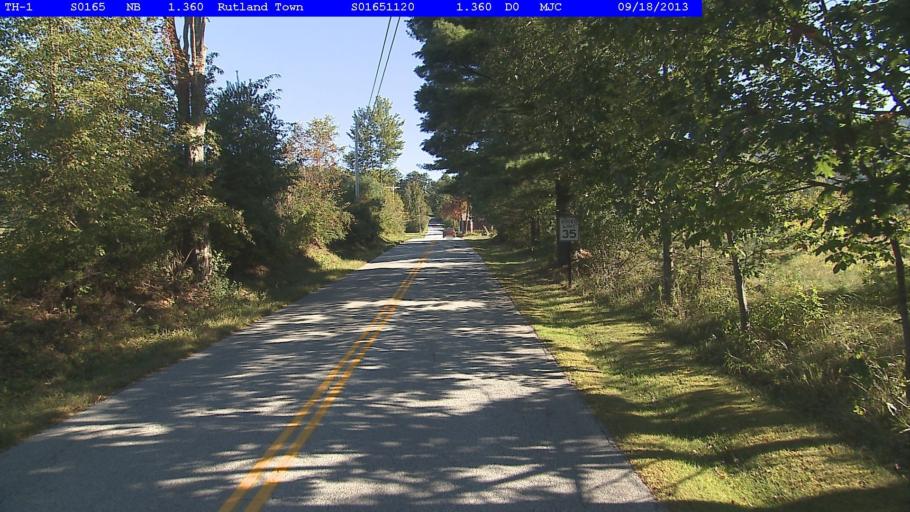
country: US
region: Vermont
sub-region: Rutland County
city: Rutland
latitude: 43.6593
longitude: -72.9512
